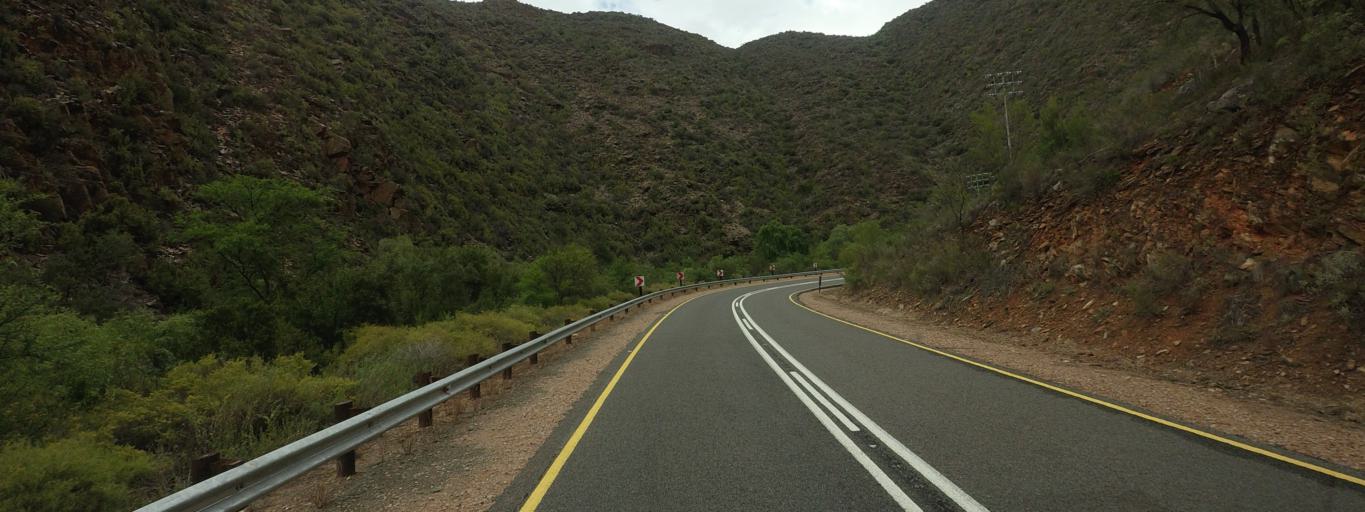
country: ZA
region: Western Cape
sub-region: Eden District Municipality
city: Oudtshoorn
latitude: -33.4267
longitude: 22.2479
